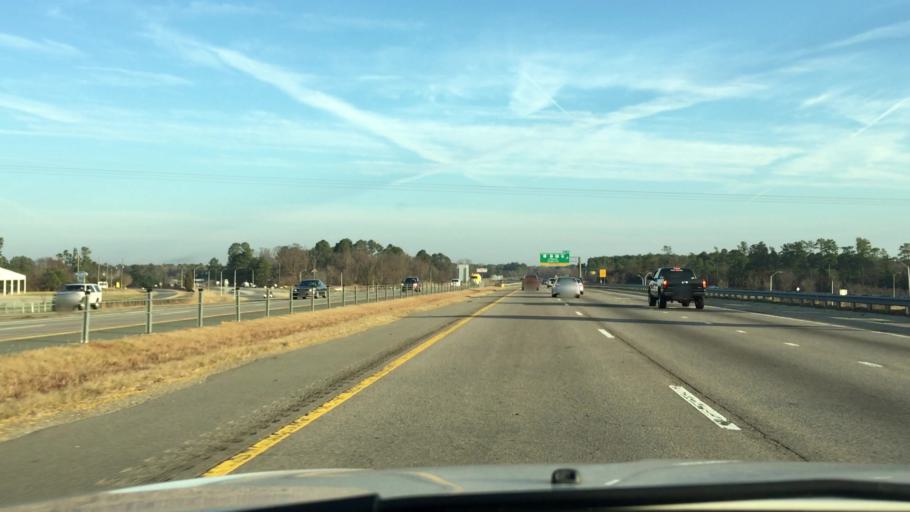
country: US
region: North Carolina
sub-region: Lee County
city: Sanford
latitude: 35.5211
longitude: -79.1845
